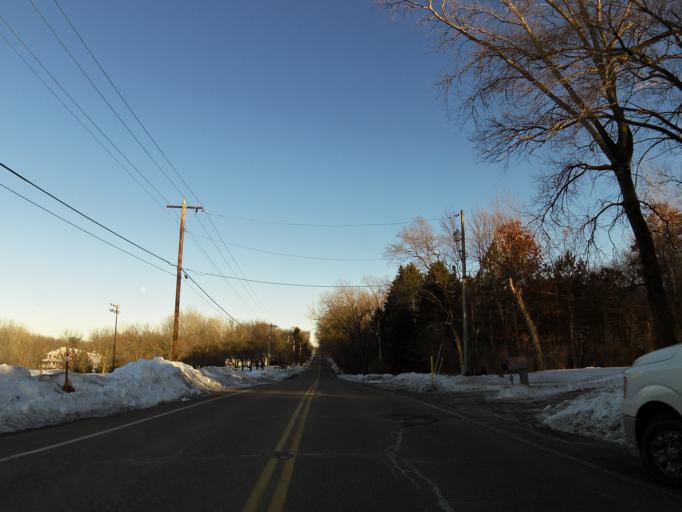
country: US
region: Minnesota
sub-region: Ramsey County
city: North Saint Paul
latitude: 45.0208
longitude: -93.0326
